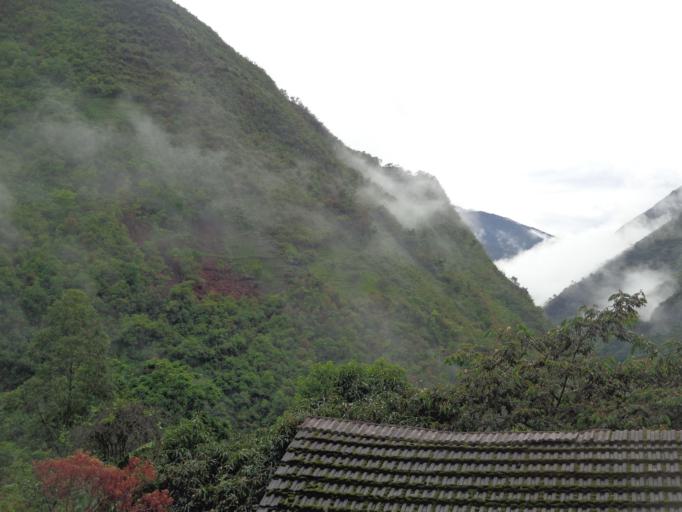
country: BO
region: La Paz
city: Coripata
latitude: -16.3983
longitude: -67.7222
